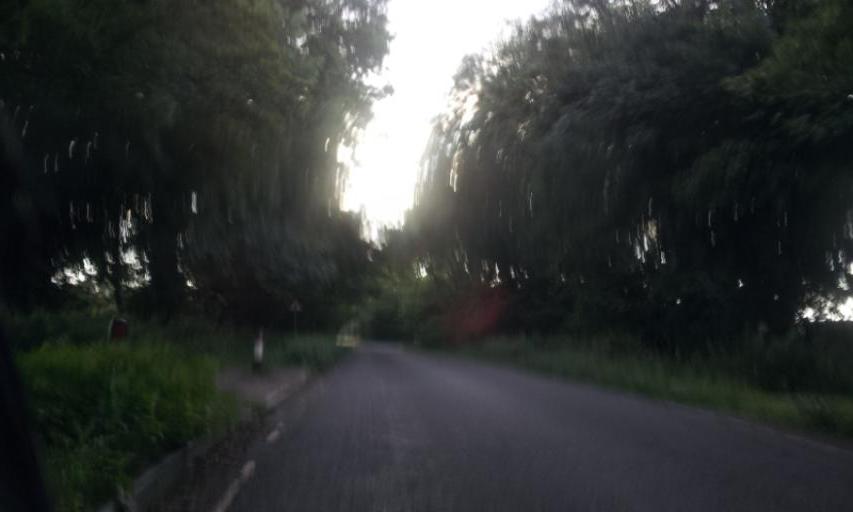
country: GB
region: England
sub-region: Kent
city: Staplehurst
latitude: 51.2233
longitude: 0.5751
